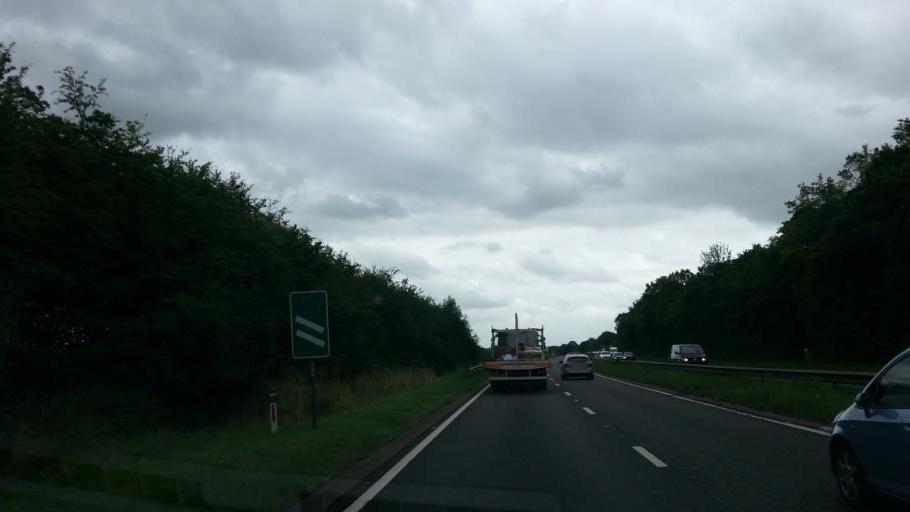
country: GB
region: England
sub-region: Warwickshire
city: Warwick
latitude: 52.2826
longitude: -1.6105
